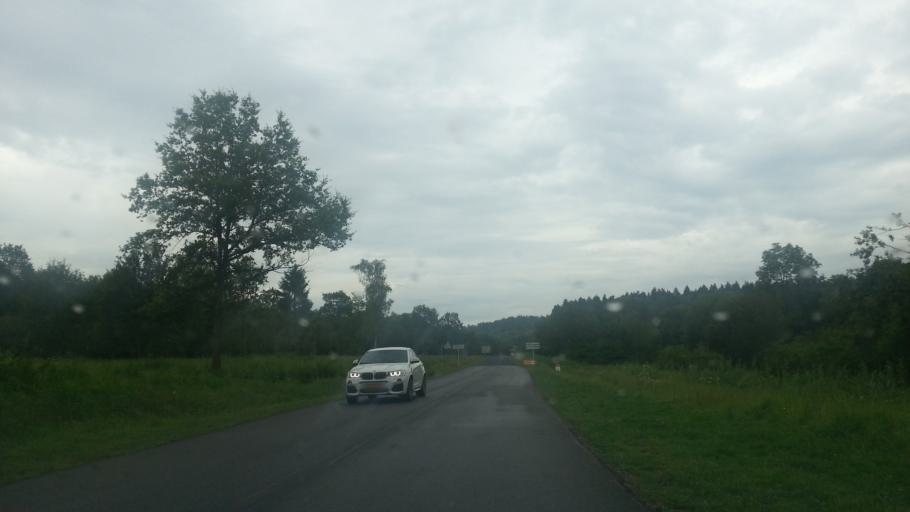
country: FR
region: Lorraine
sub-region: Departement de la Meuse
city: Verdun
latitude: 49.1945
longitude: 5.4350
